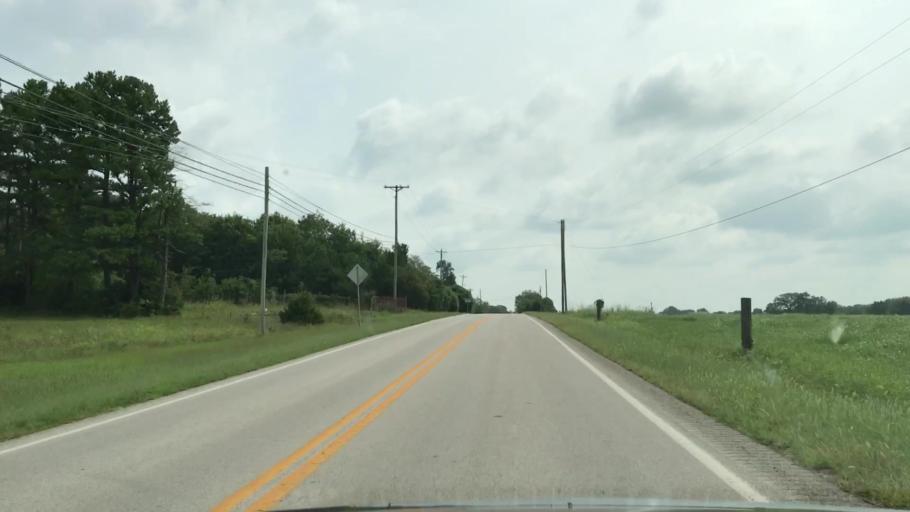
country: US
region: Kentucky
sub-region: Barren County
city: Cave City
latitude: 37.0903
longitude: -86.0695
